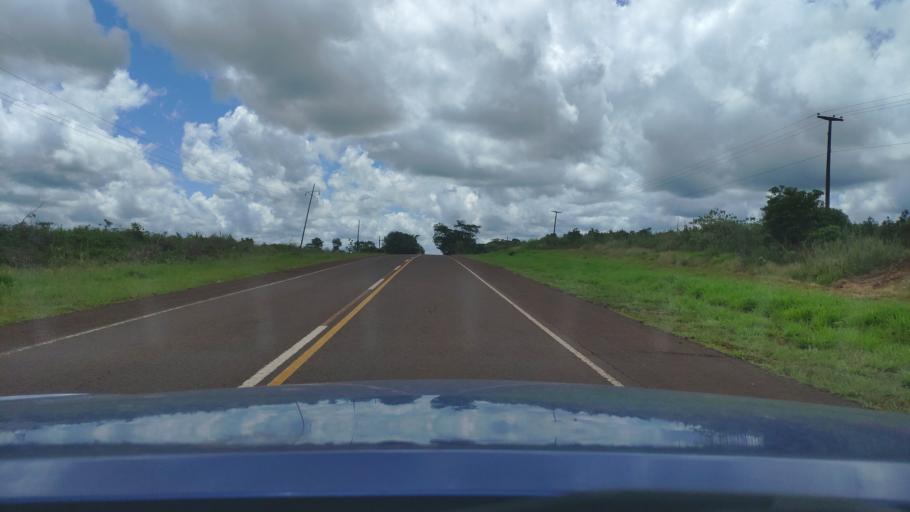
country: AR
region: Misiones
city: Picada Gobernador Lopez
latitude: -27.6542
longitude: -55.2823
